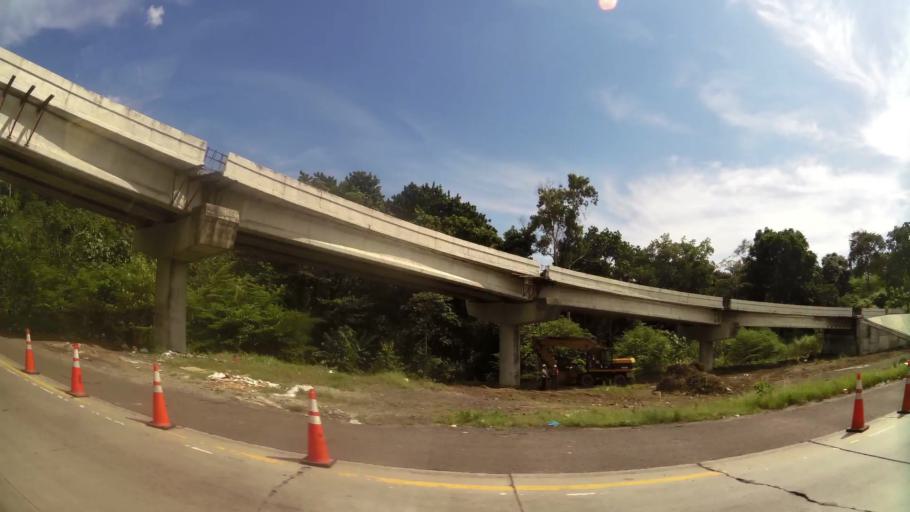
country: PA
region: Panama
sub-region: Distrito de Panama
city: Paraiso
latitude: 9.0352
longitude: -79.5776
